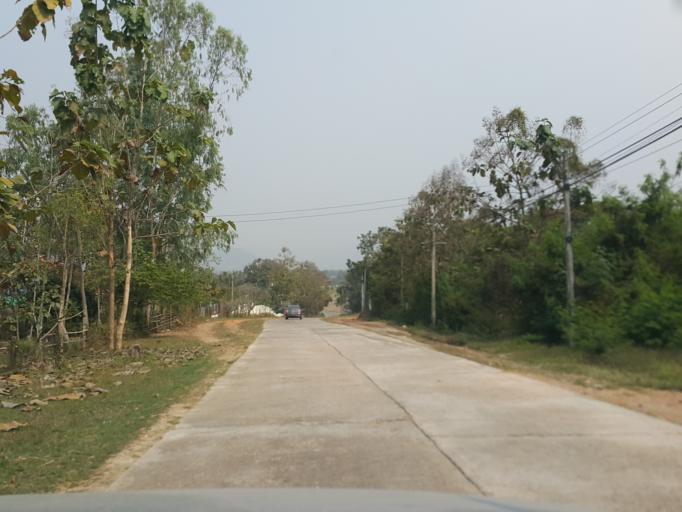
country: TH
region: Lampang
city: Thoen
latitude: 17.6365
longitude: 99.2498
